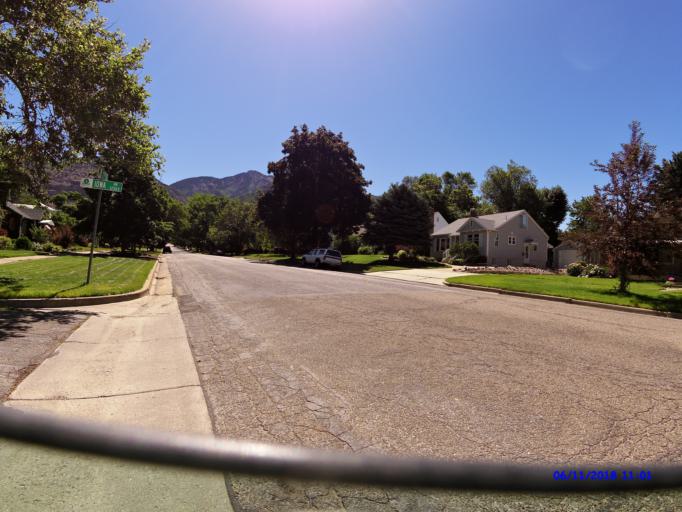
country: US
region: Utah
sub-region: Weber County
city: Ogden
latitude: 41.2162
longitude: -111.9473
